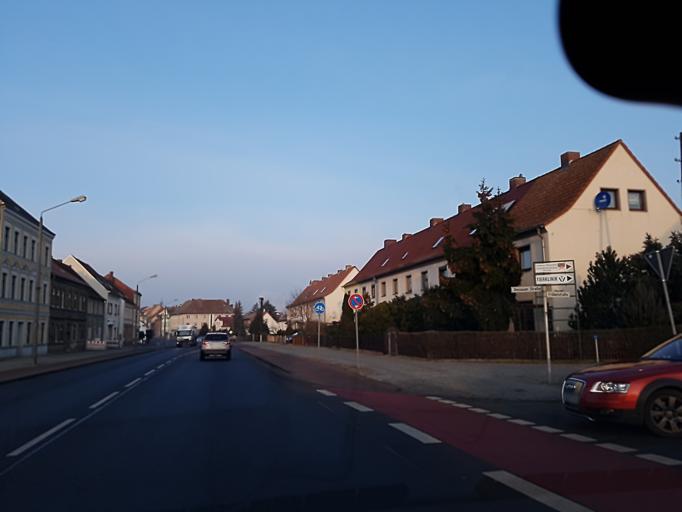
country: DE
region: Saxony-Anhalt
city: Wittenburg
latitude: 51.8671
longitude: 12.6050
